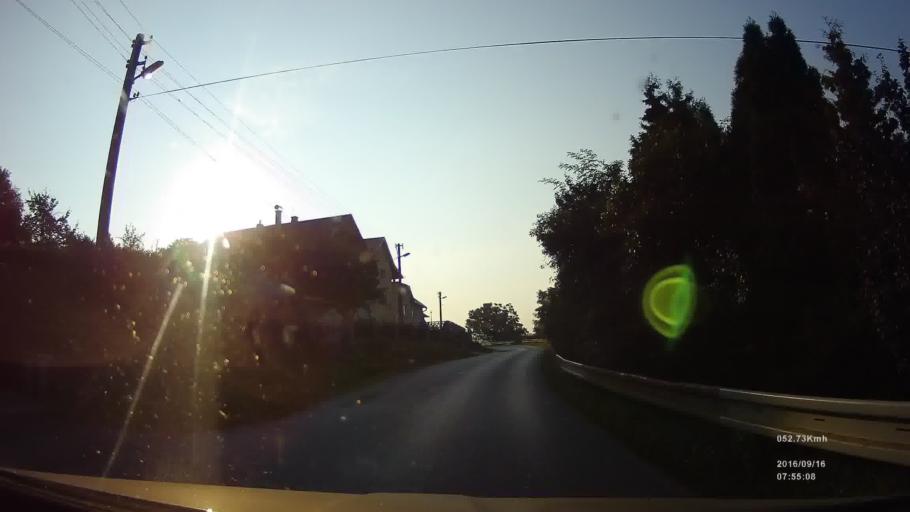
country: SK
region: Presovsky
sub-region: Okres Presov
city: Presov
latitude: 48.9157
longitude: 21.1233
